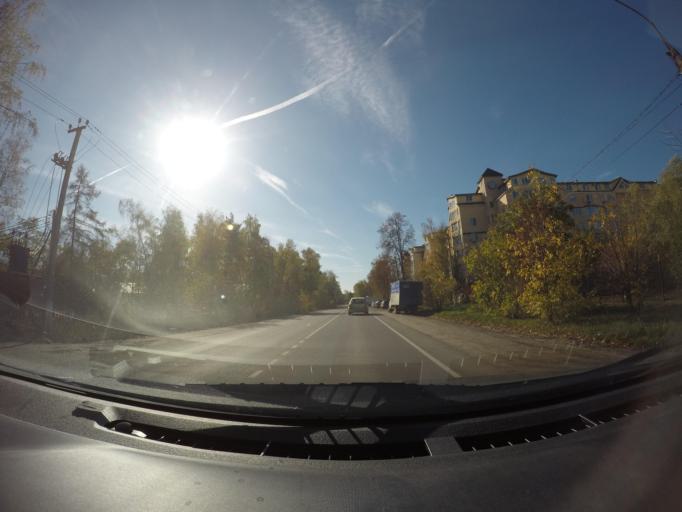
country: RU
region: Moskovskaya
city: Rodniki
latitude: 55.6505
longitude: 38.0565
